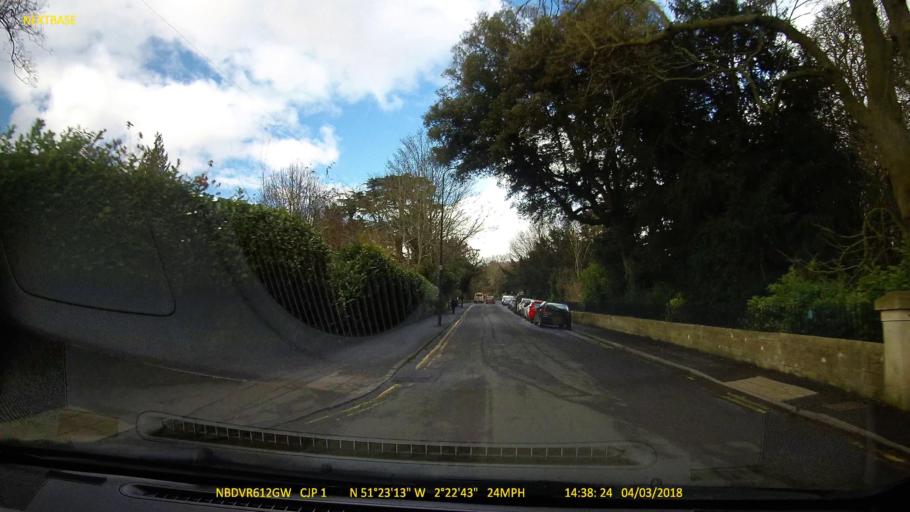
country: GB
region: England
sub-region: Bath and North East Somerset
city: Bath
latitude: 51.3874
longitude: -2.3787
